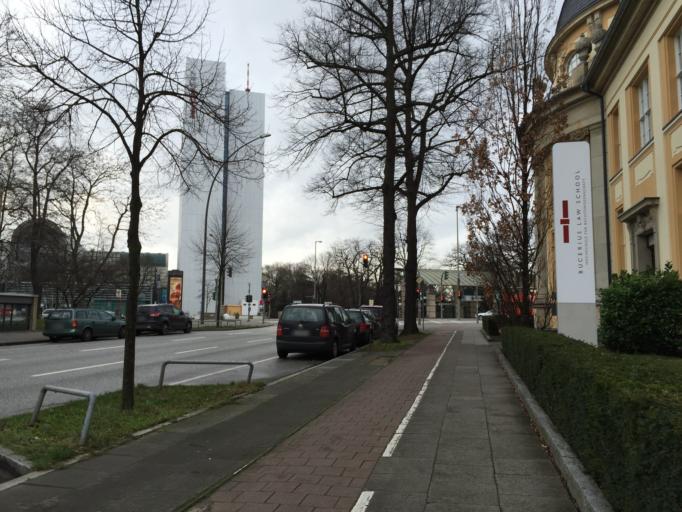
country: DE
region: Hamburg
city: Eimsbuettel
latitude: 53.5592
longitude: 9.9827
